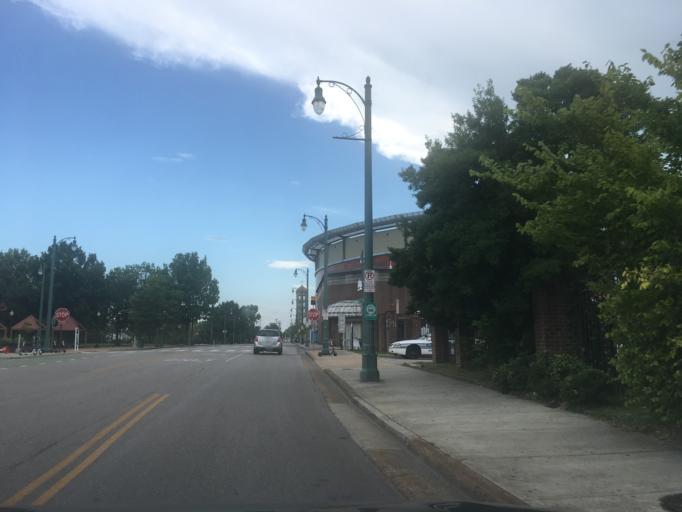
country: US
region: Tennessee
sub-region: Shelby County
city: Memphis
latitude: 35.1399
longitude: -90.0494
